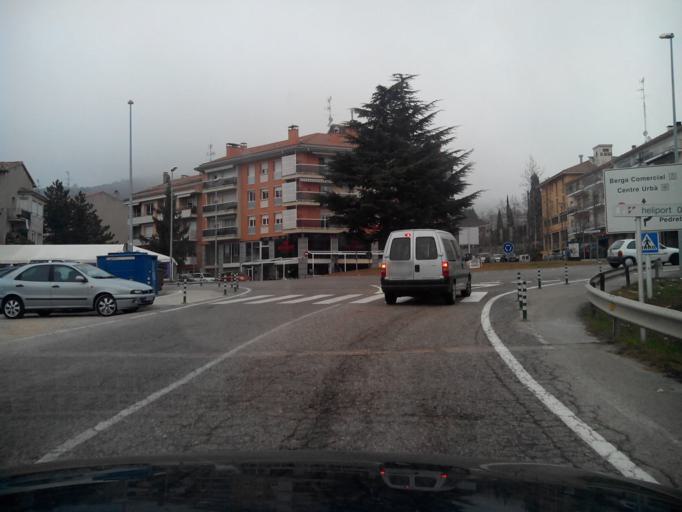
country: ES
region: Catalonia
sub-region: Provincia de Barcelona
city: Berga
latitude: 42.1017
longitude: 1.8573
